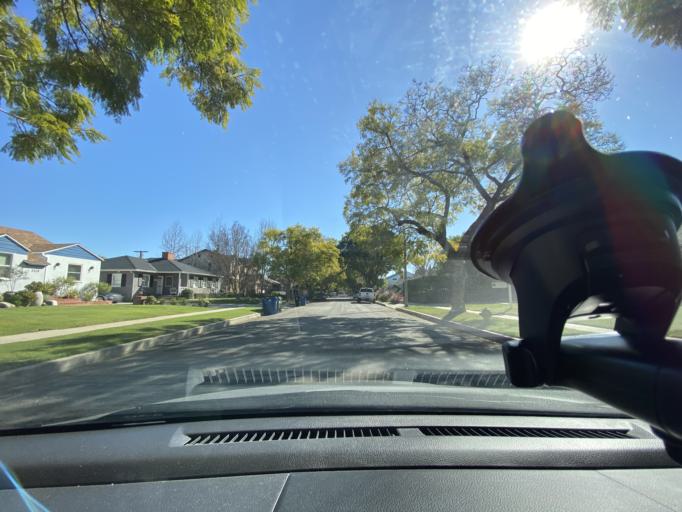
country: US
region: California
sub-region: Los Angeles County
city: Westwood, Los Angeles
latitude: 34.0231
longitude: -118.4337
